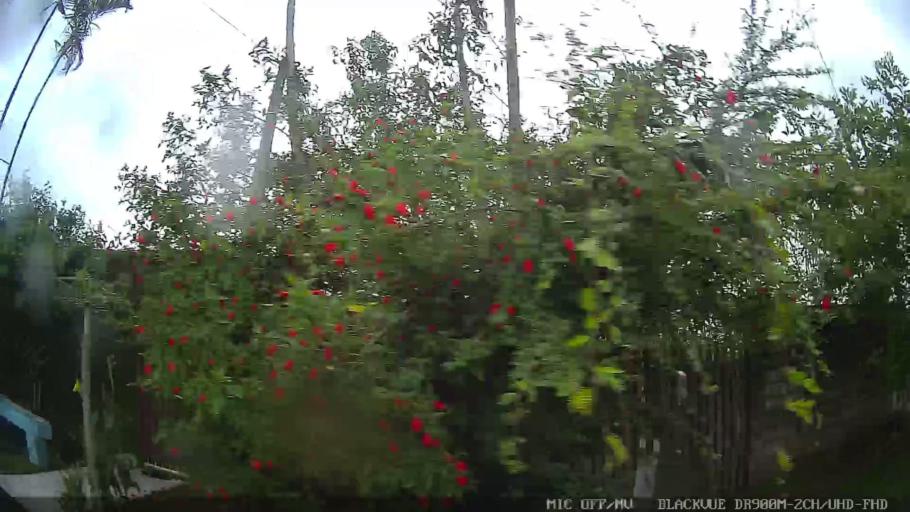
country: BR
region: Sao Paulo
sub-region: Itanhaem
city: Itanhaem
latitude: -24.1652
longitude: -46.7724
